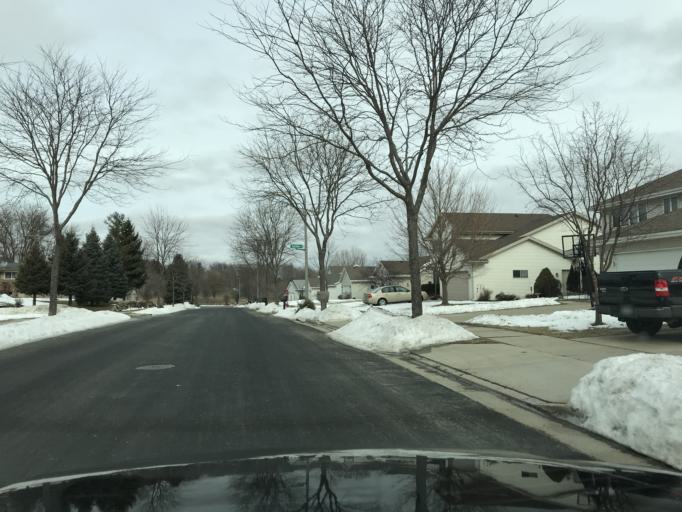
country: US
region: Wisconsin
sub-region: Dane County
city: Monona
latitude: 43.0922
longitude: -89.2692
